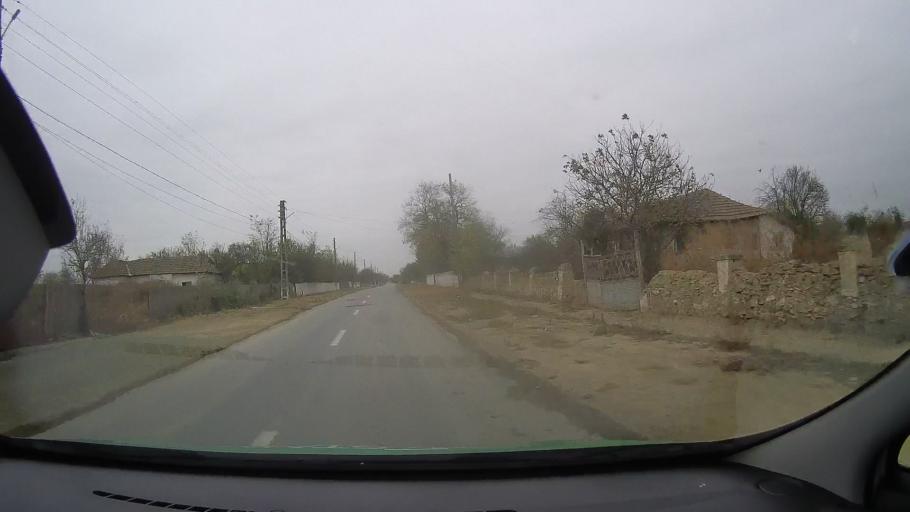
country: RO
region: Constanta
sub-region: Comuna Vulturu
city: Vulturu
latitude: 44.6422
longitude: 28.2732
